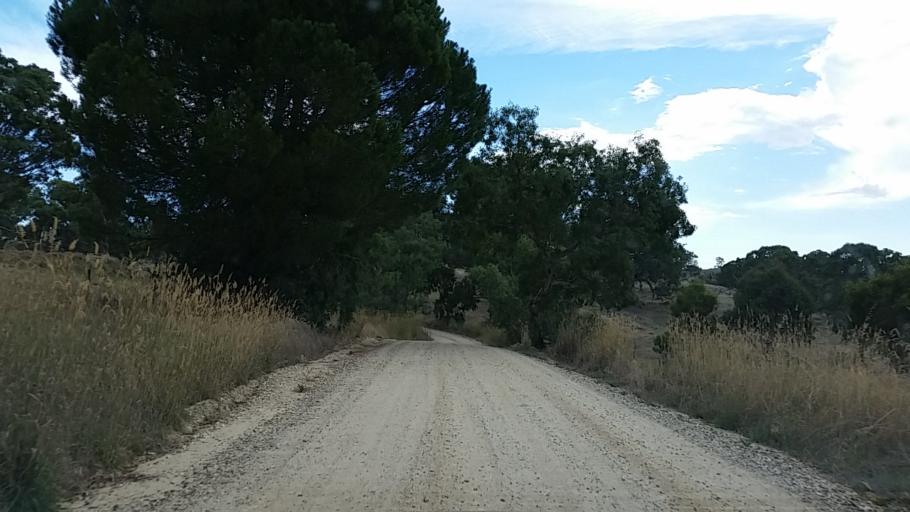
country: AU
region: South Australia
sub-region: Barossa
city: Angaston
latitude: -34.5628
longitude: 139.0752
